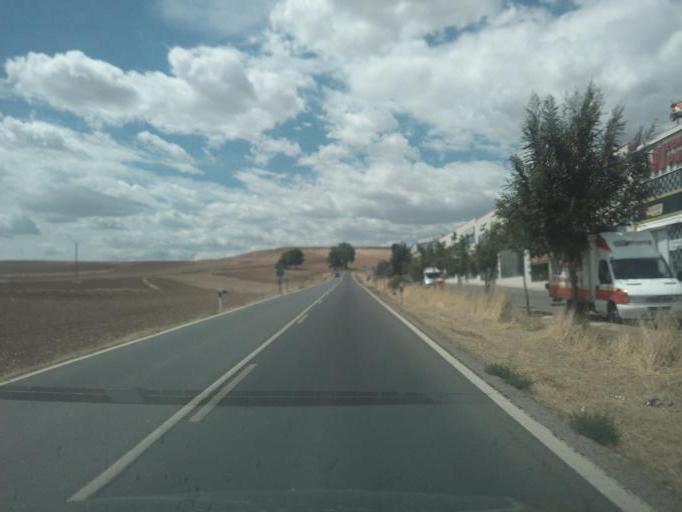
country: ES
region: Madrid
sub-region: Provincia de Madrid
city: Ajalvir
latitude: 40.5299
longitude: -3.4830
